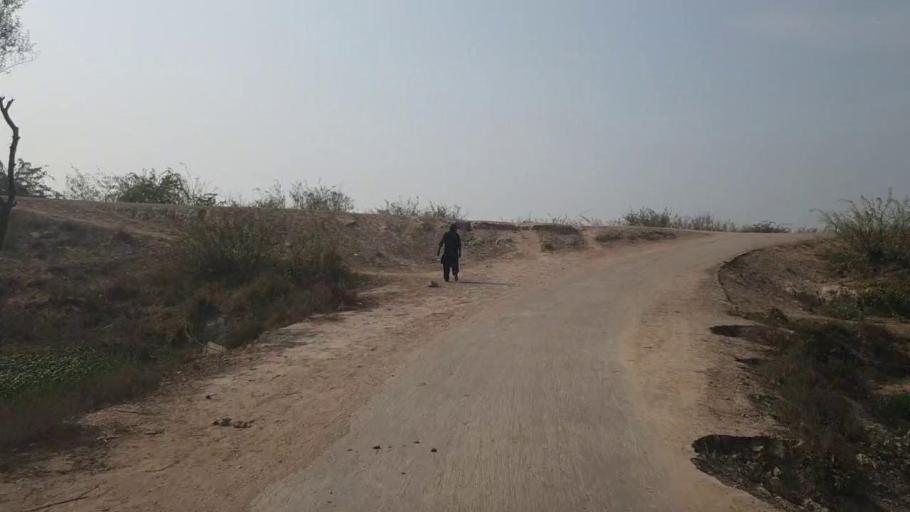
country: PK
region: Sindh
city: Hala
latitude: 25.8114
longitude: 68.4018
